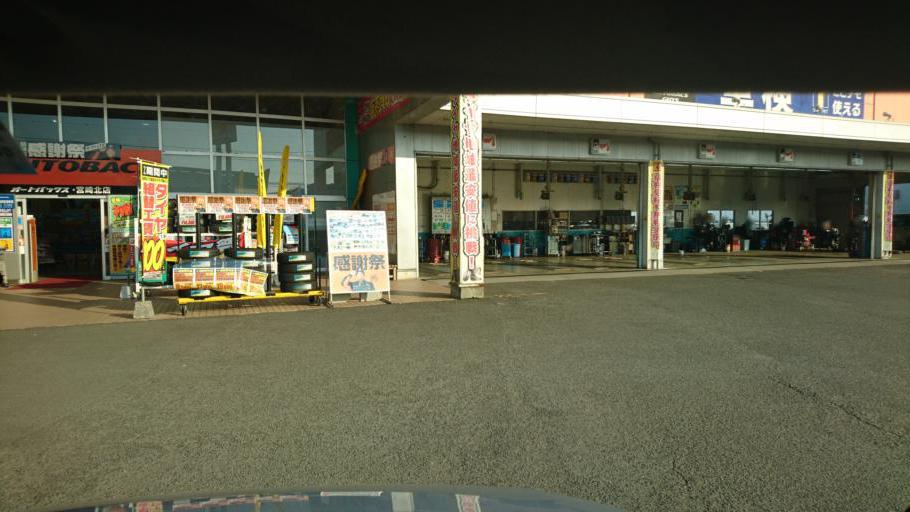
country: JP
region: Miyazaki
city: Miyazaki-shi
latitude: 31.9814
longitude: 131.4470
